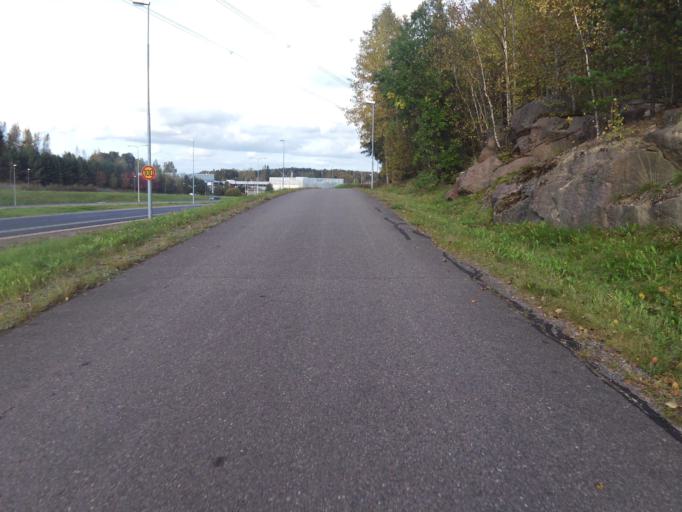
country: FI
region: Uusimaa
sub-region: Helsinki
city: Kauniainen
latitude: 60.2618
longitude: 24.7354
